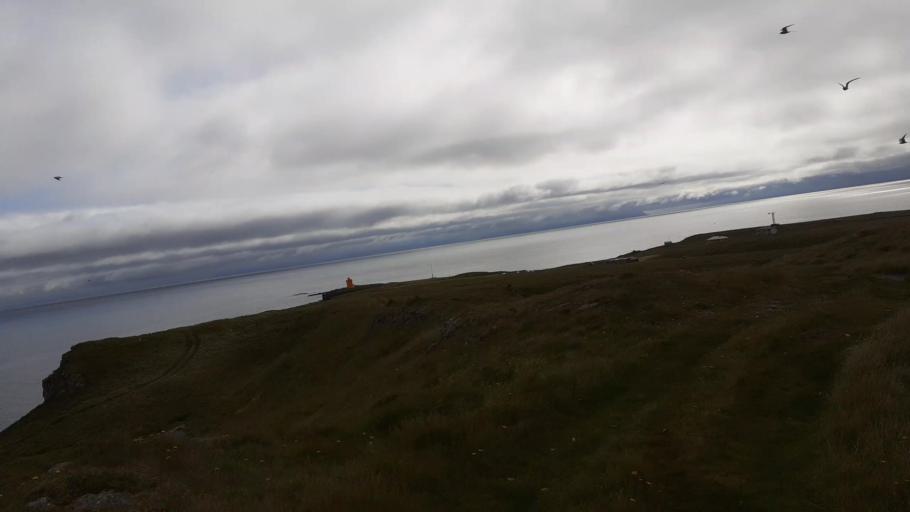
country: IS
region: Northeast
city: Dalvik
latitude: 66.5334
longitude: -17.9827
